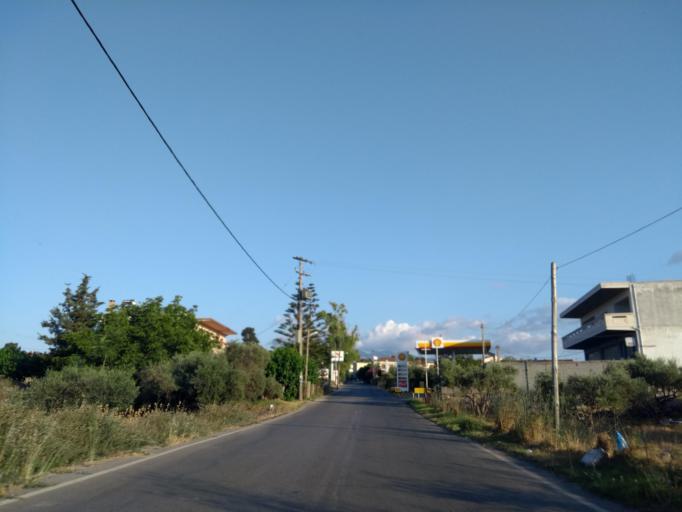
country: GR
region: Crete
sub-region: Nomos Chanias
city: Kalivai
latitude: 35.4122
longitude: 24.1957
